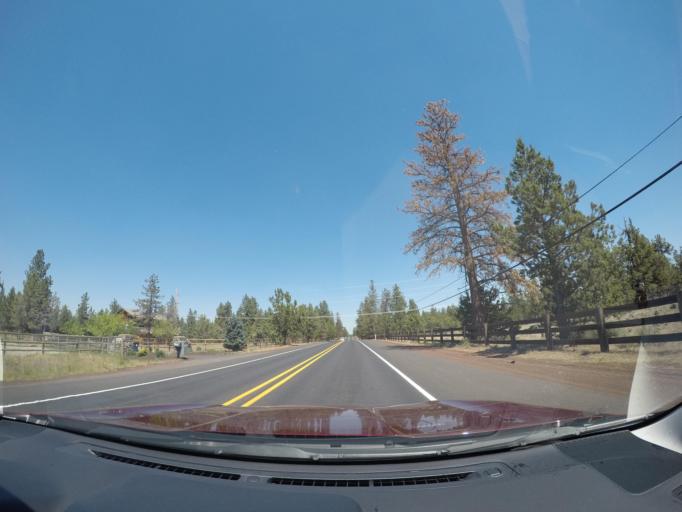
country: US
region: Oregon
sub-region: Deschutes County
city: Sisters
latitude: 44.2888
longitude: -121.5030
